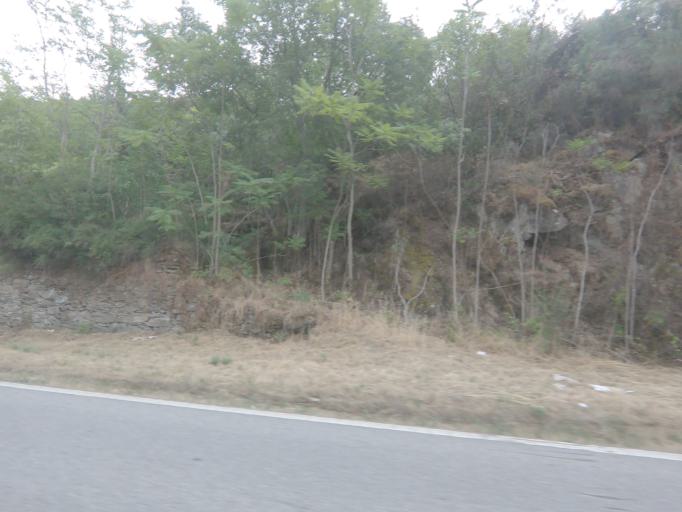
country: PT
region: Viseu
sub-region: Tabuaco
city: Tabuaco
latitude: 41.1585
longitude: -7.5767
